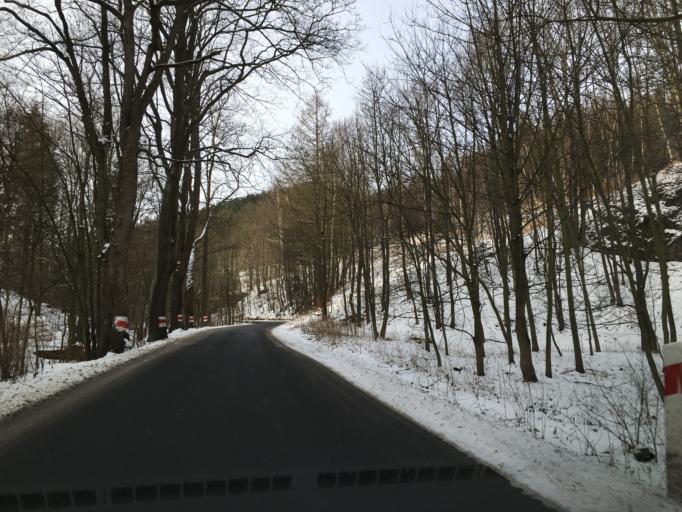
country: PL
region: Lower Silesian Voivodeship
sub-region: Powiat walbrzyski
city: Jedlina-Zdroj
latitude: 50.7032
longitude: 16.3107
